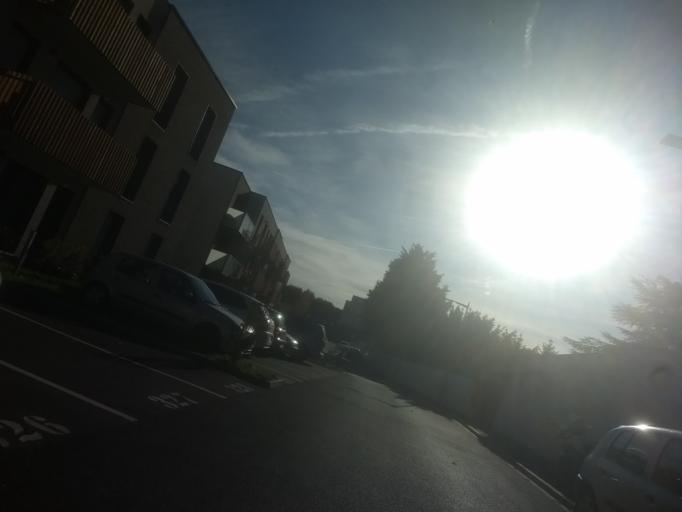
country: FR
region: Nord-Pas-de-Calais
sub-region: Departement du Pas-de-Calais
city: Arras
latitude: 50.2886
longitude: 2.7878
